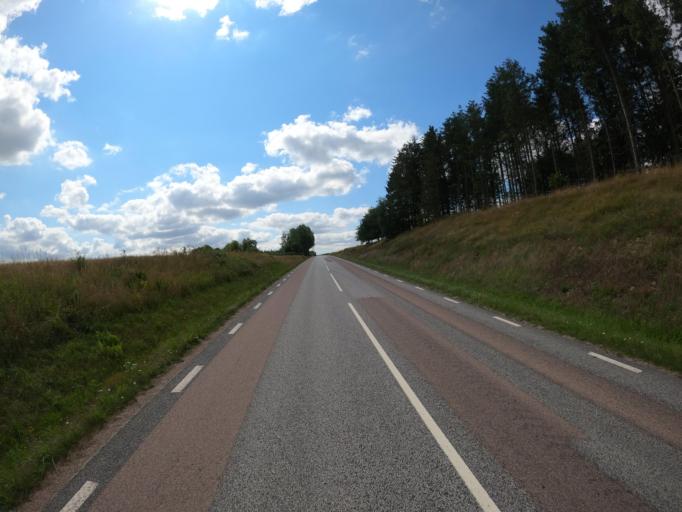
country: SE
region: Skane
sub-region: Lunds Kommun
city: Veberod
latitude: 55.6112
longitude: 13.4906
